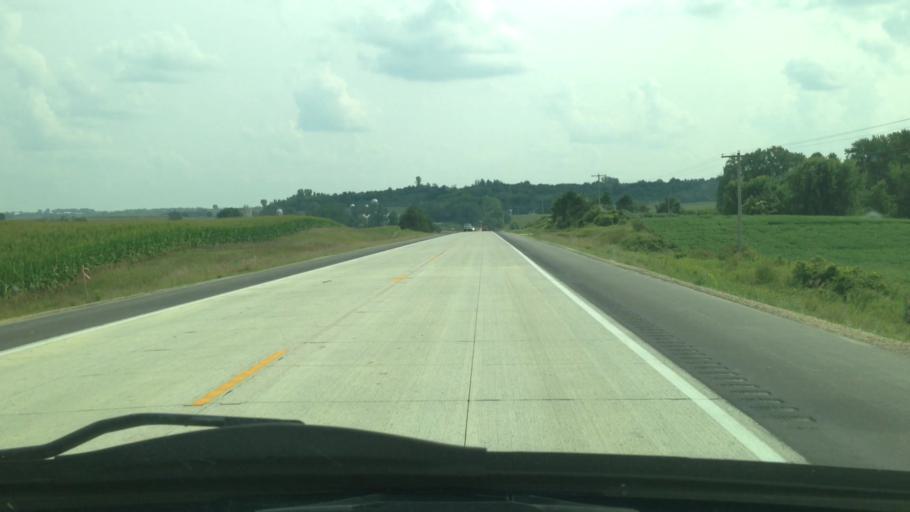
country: US
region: Minnesota
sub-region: Olmsted County
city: Oronoco
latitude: 44.1542
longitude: -92.4194
